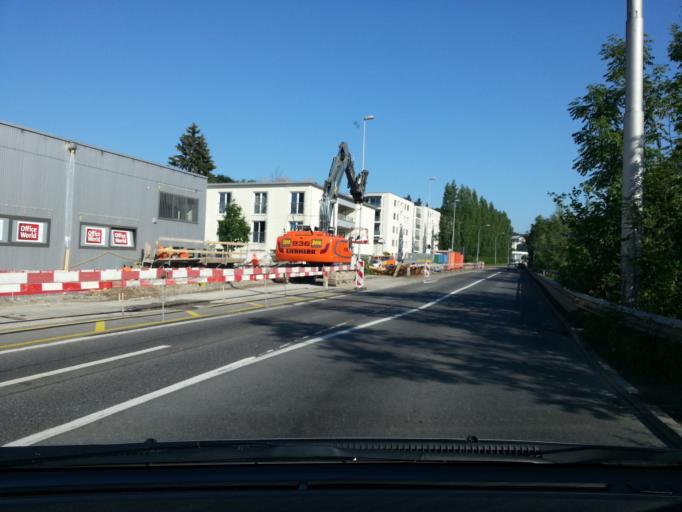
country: CH
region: Lucerne
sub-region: Hochdorf District
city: Emmen
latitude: 47.0680
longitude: 8.2796
